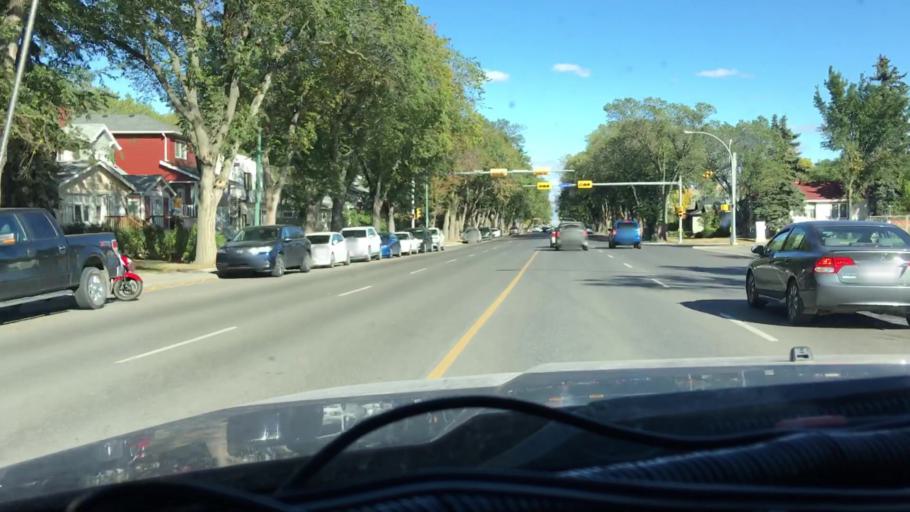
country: CA
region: Saskatchewan
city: Regina
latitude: 50.4551
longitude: -104.6366
